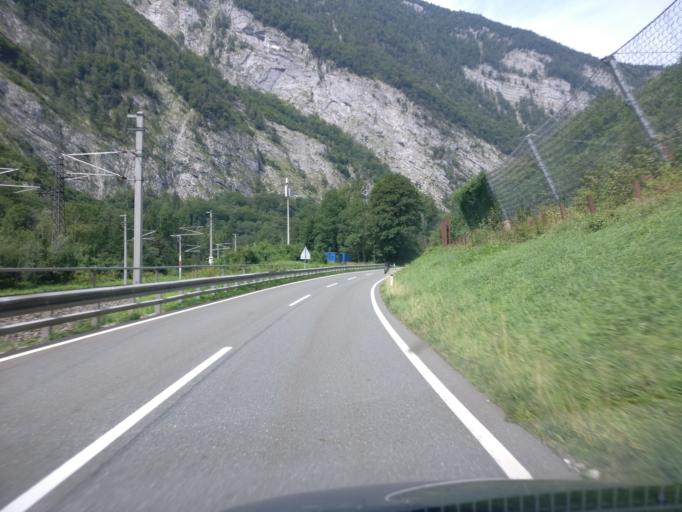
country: AT
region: Salzburg
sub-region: Politischer Bezirk Hallein
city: Golling an der Salzach
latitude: 47.5542
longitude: 13.1682
